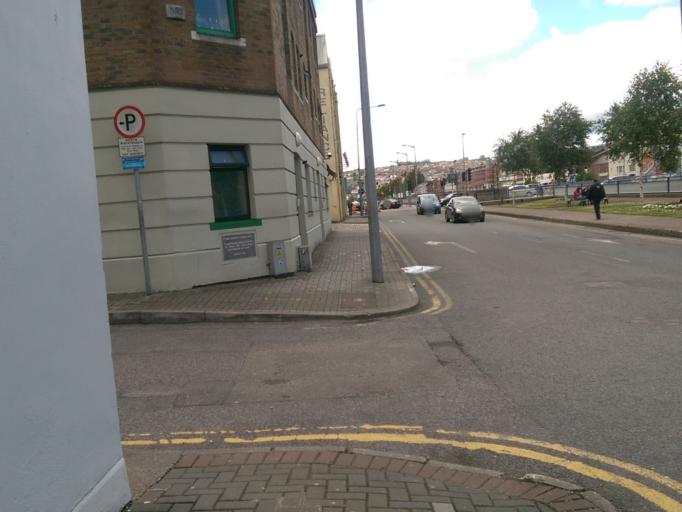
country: IE
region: Munster
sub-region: County Cork
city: Cork
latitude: 51.8997
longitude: -8.4647
